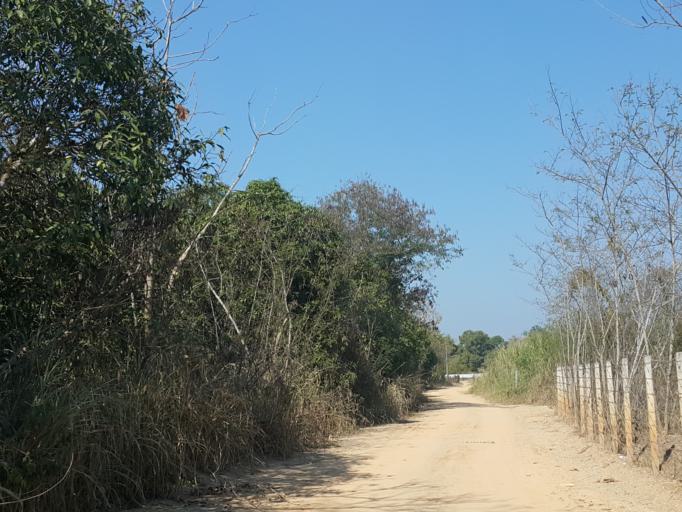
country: TH
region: Chiang Mai
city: San Sai
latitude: 18.9307
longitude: 99.0014
